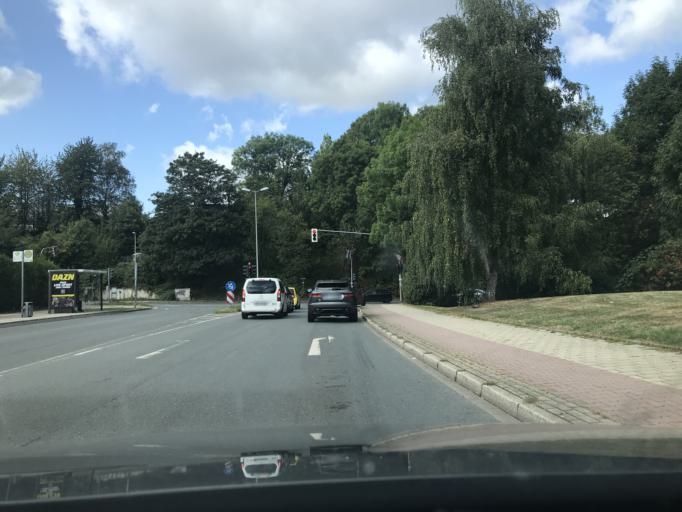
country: DE
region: North Rhine-Westphalia
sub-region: Regierungsbezirk Dusseldorf
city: Erkrath
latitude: 51.2194
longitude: 6.9137
